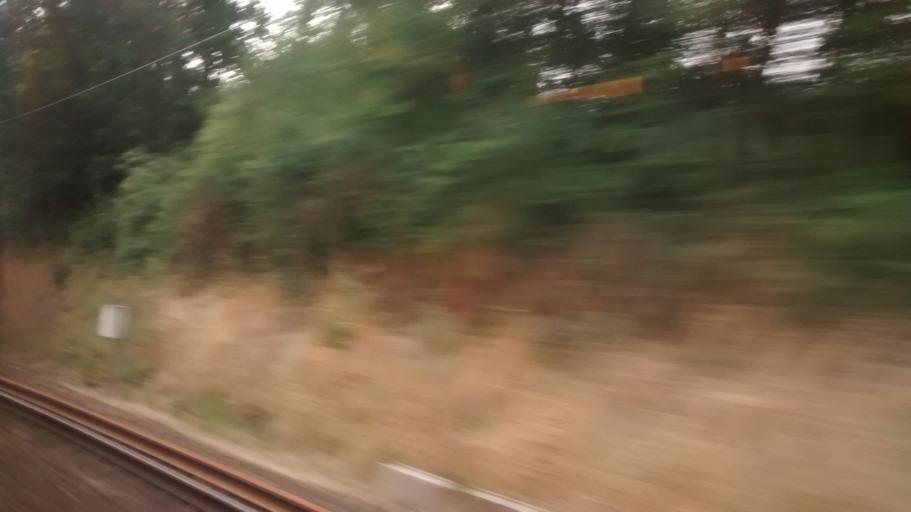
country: FR
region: Pays de la Loire
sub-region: Departement de la Mayenne
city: Louverne
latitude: 48.1208
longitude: -0.6895
